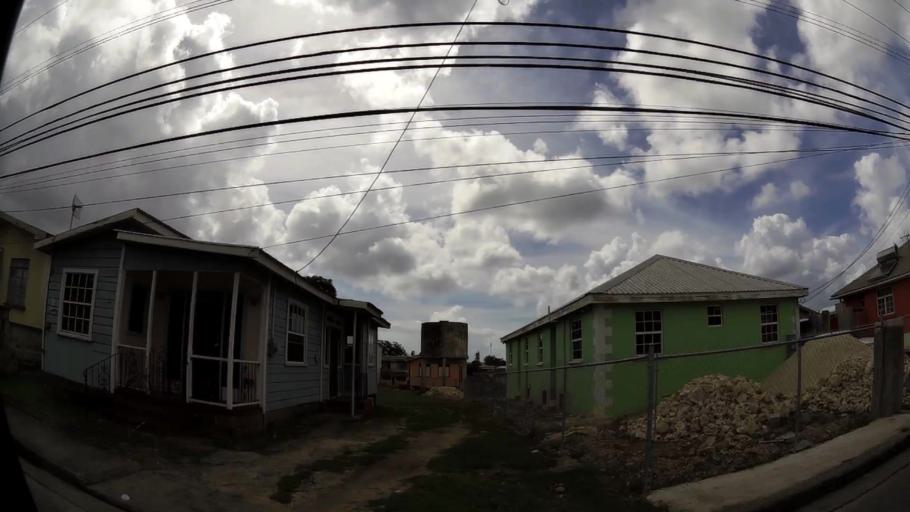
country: BB
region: Saint Michael
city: Bridgetown
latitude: 13.1245
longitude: -59.6087
